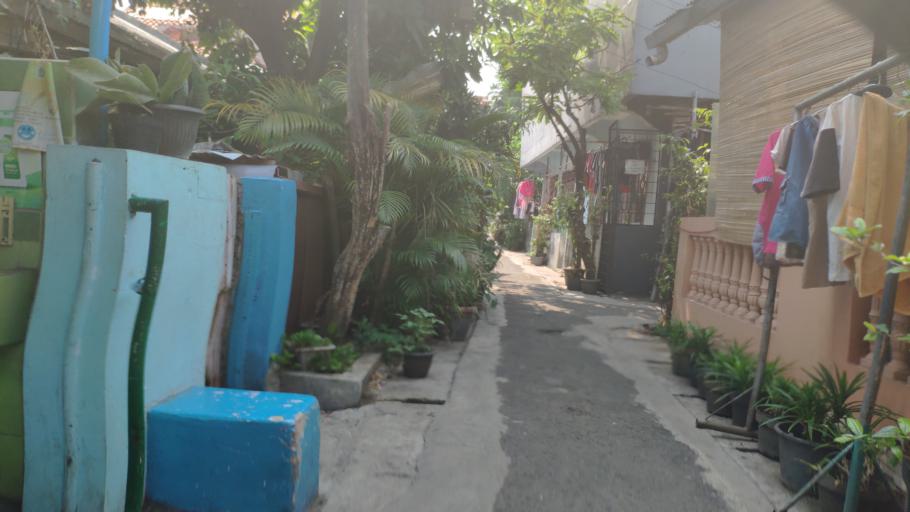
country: ID
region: Jakarta Raya
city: Jakarta
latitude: -6.2523
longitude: 106.7935
